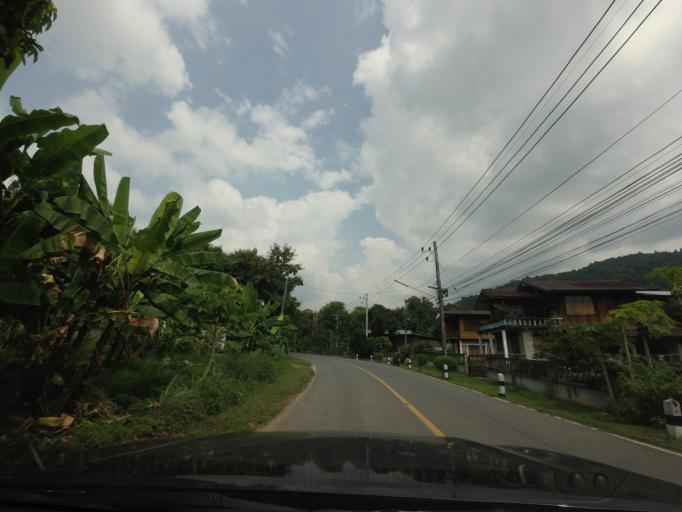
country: TH
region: Nan
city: Pua
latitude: 19.1758
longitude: 100.9566
